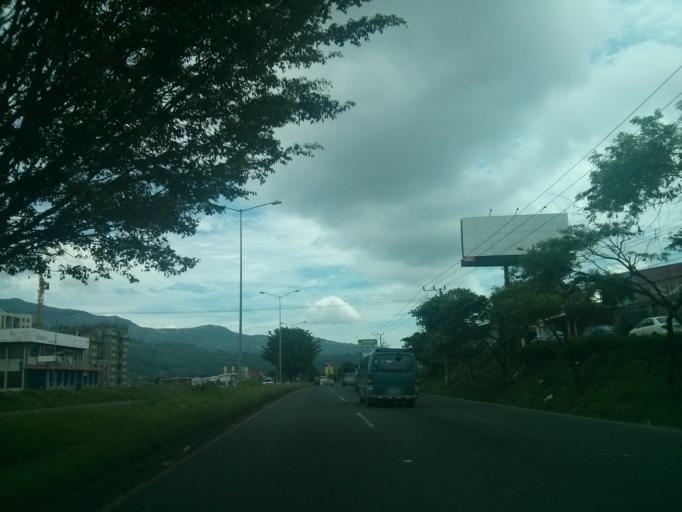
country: CR
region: San Jose
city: Alajuelita
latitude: 9.9104
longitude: -84.0918
